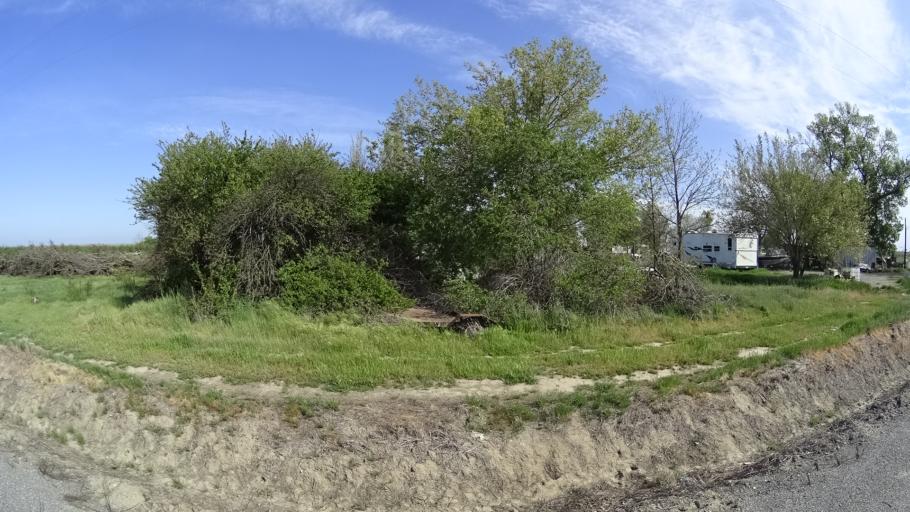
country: US
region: California
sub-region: Glenn County
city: Hamilton City
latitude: 39.6270
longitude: -122.0380
